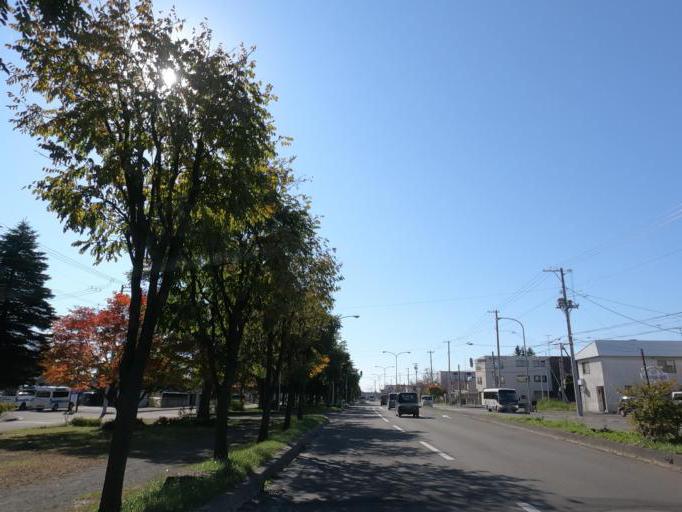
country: JP
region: Hokkaido
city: Obihiro
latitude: 42.9087
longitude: 143.2138
